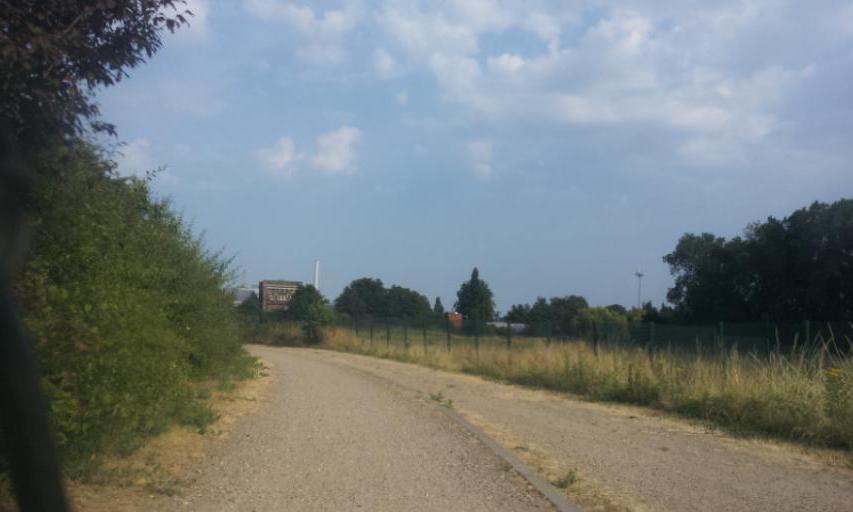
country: GB
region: England
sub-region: Greater London
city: Belvedere
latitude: 51.5109
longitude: 0.1343
